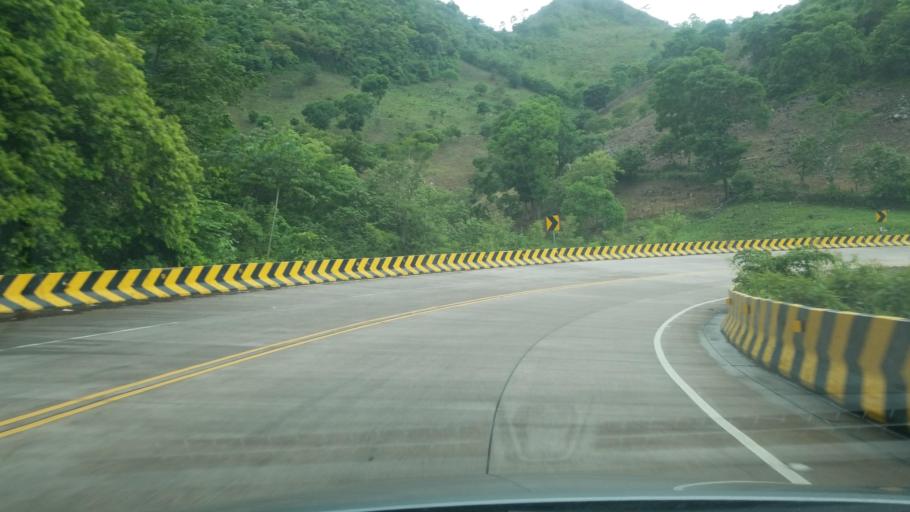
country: HN
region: Copan
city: Copan
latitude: 14.8533
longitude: -89.2165
